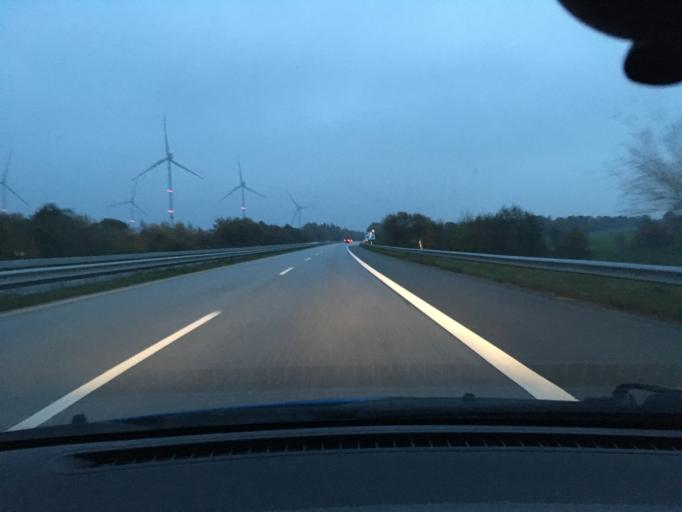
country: DE
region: Schleswig-Holstein
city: Arkebek
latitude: 54.1441
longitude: 9.2457
